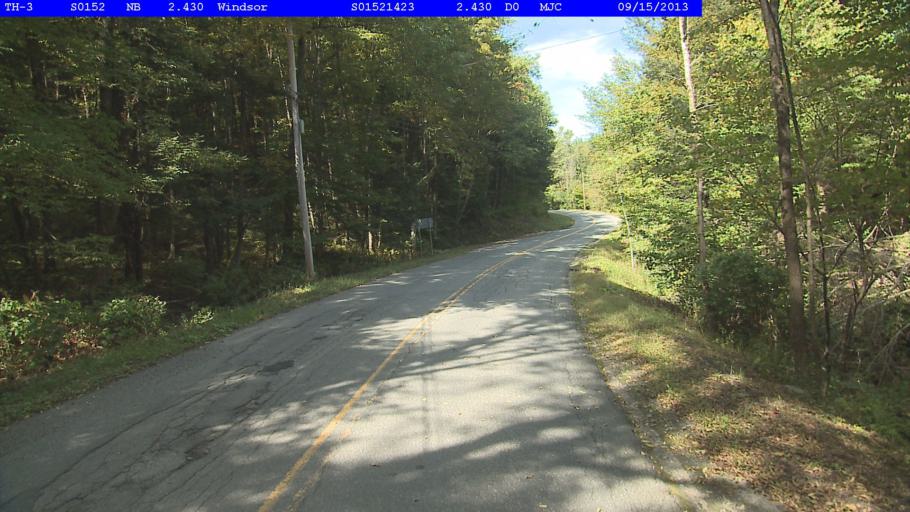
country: US
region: Vermont
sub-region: Windsor County
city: Windsor
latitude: 43.5019
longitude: -72.4186
